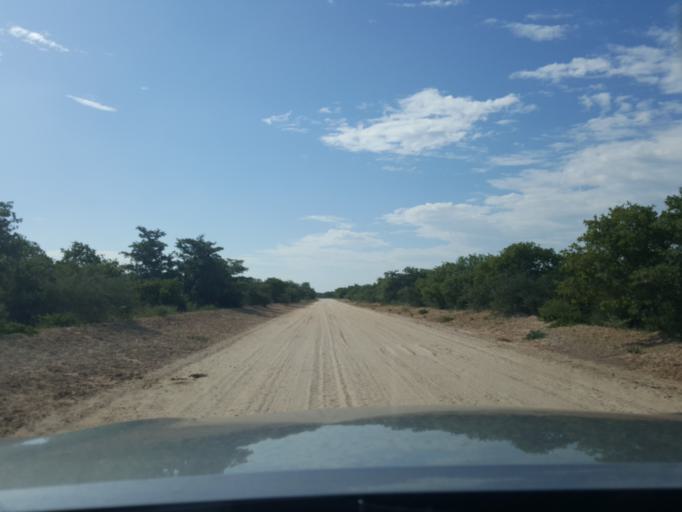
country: BW
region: Kweneng
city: Khudumelapye
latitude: -23.4953
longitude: 24.7023
